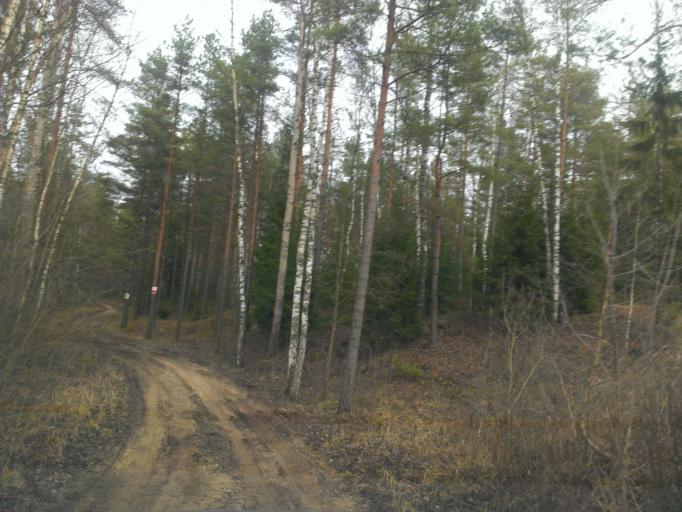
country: LV
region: Riga
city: Bergi
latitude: 56.9962
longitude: 24.3404
